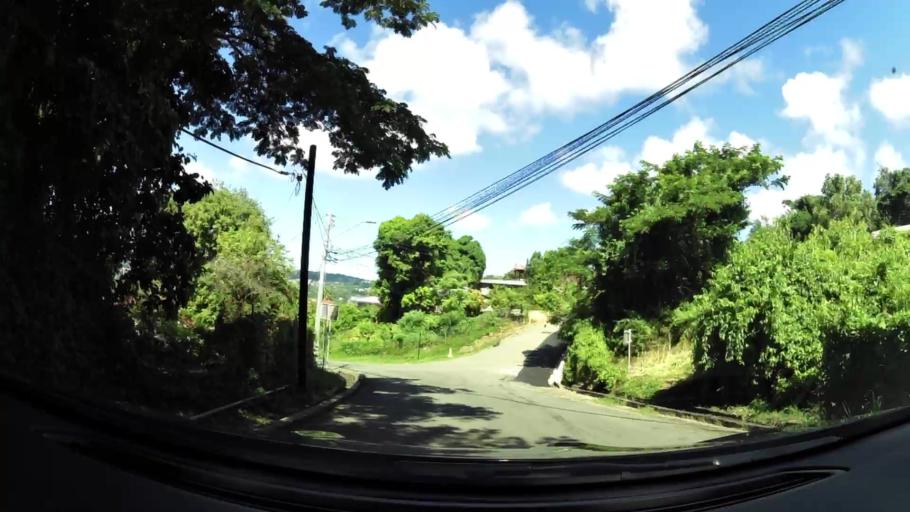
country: TT
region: Tobago
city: Scarborough
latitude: 11.1810
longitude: -60.7295
